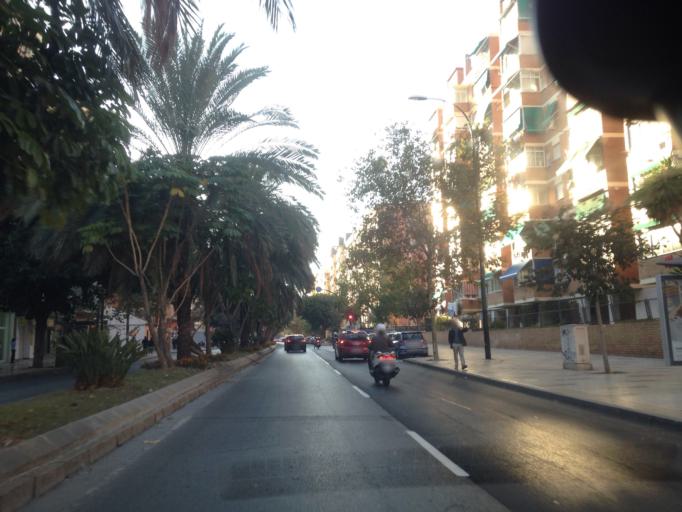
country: ES
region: Andalusia
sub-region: Provincia de Malaga
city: Malaga
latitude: 36.7110
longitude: -4.4480
